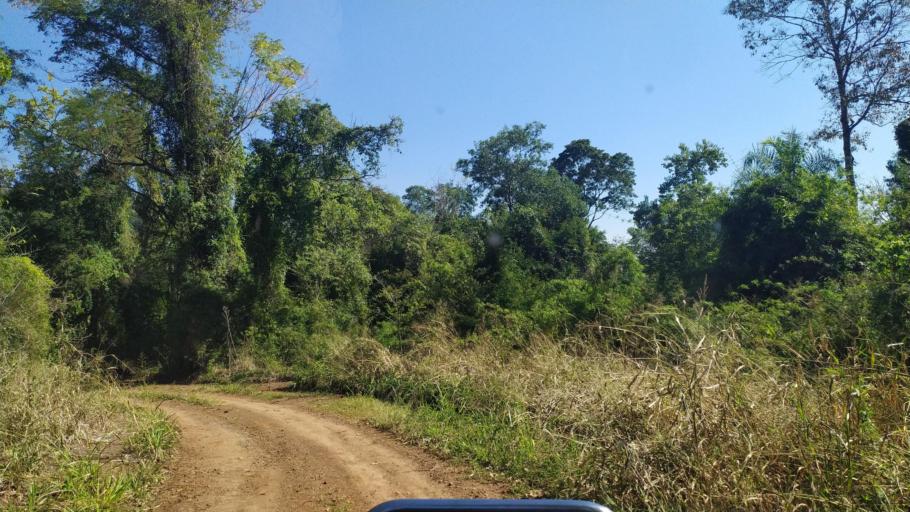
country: AR
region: Misiones
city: El Alcazar
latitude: -26.7585
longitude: -54.5811
